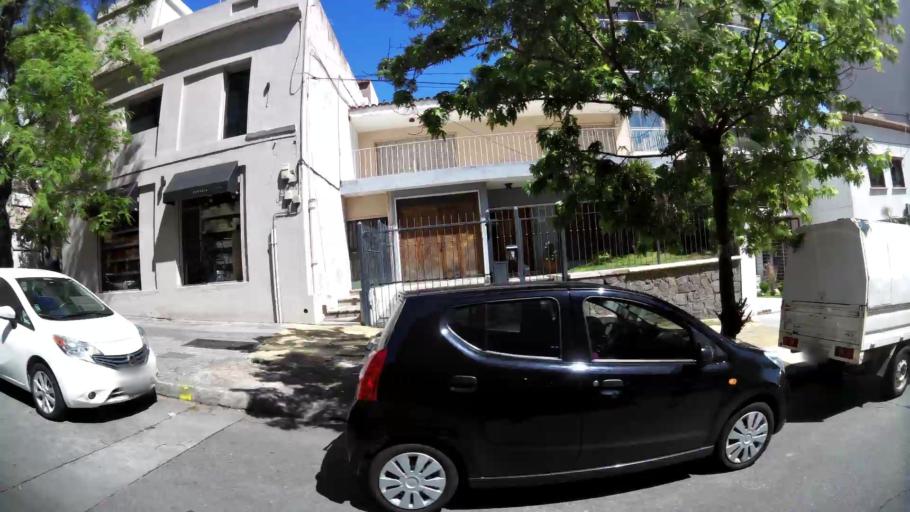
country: UY
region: Montevideo
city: Montevideo
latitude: -34.9067
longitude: -56.1413
